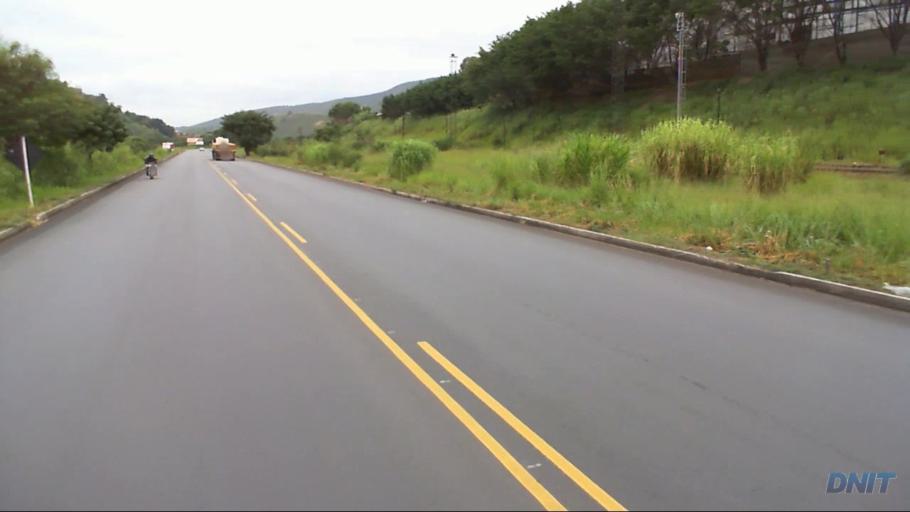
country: BR
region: Minas Gerais
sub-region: Coronel Fabriciano
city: Coronel Fabriciano
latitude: -19.5259
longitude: -42.6383
